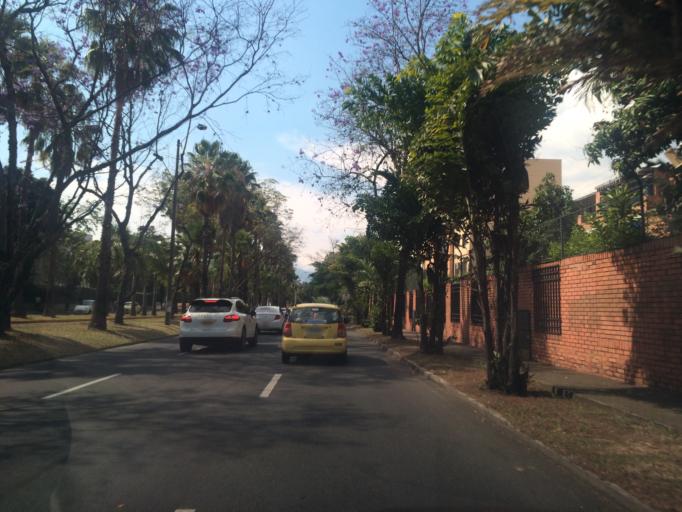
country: CO
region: Valle del Cauca
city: Cali
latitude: 3.3809
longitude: -76.5377
